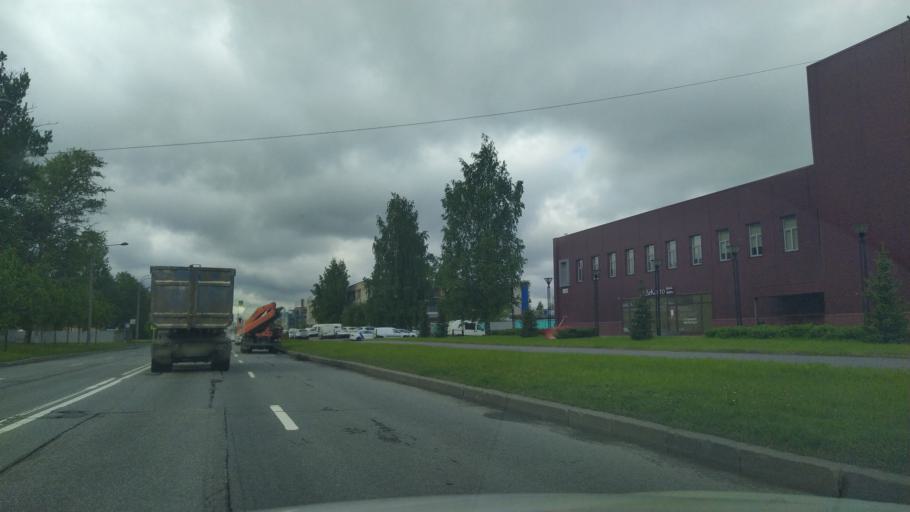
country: RU
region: St.-Petersburg
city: Krasnogvargeisky
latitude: 59.9695
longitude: 30.4759
